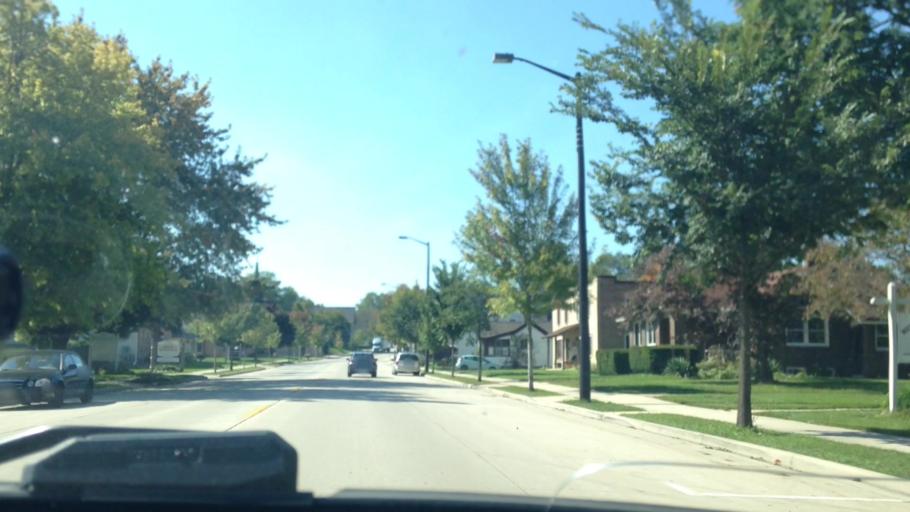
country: US
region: Wisconsin
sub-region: Ozaukee County
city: Port Washington
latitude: 43.3873
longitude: -87.8773
